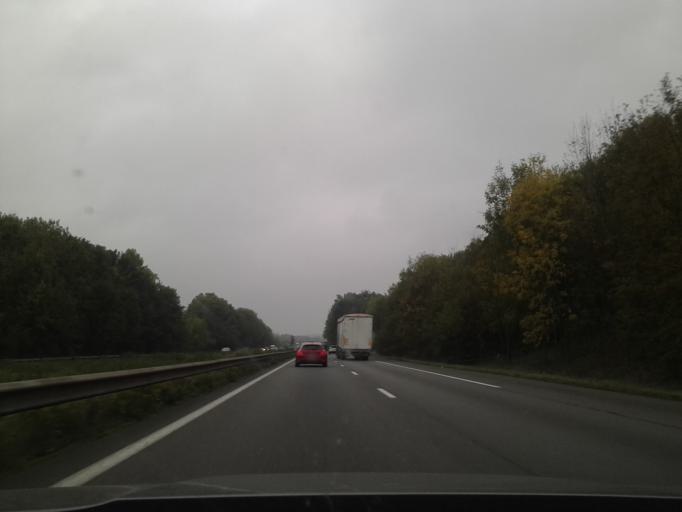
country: FR
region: Nord-Pas-de-Calais
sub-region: Departement du Nord
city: Haulchin
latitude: 50.3296
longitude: 3.4390
